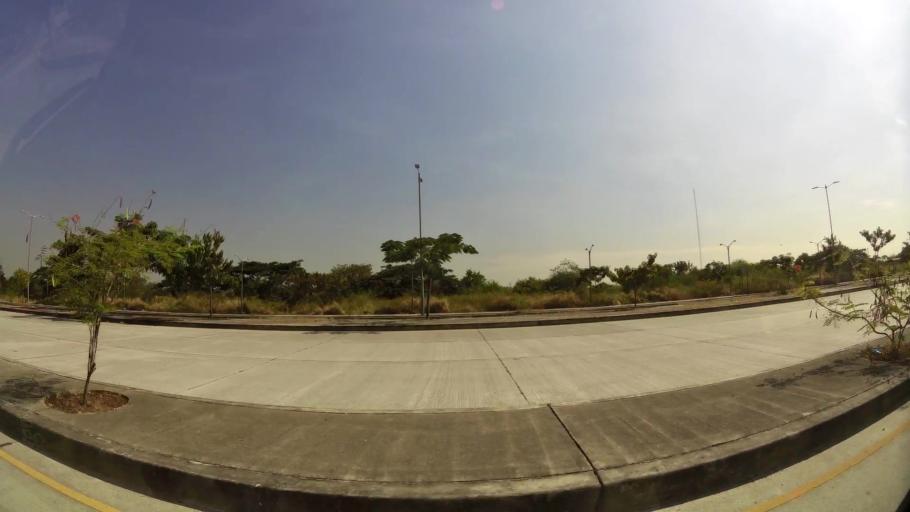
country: EC
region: Guayas
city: Eloy Alfaro
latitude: -2.1010
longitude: -79.9015
